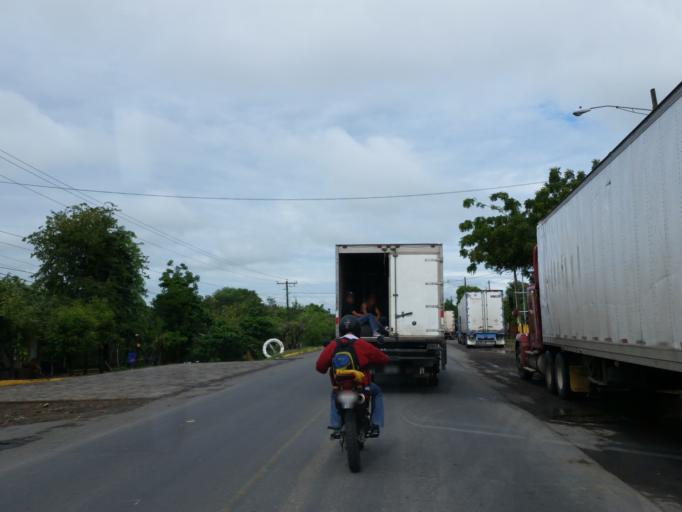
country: NI
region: Leon
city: Nagarote
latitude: 12.2704
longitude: -86.5575
